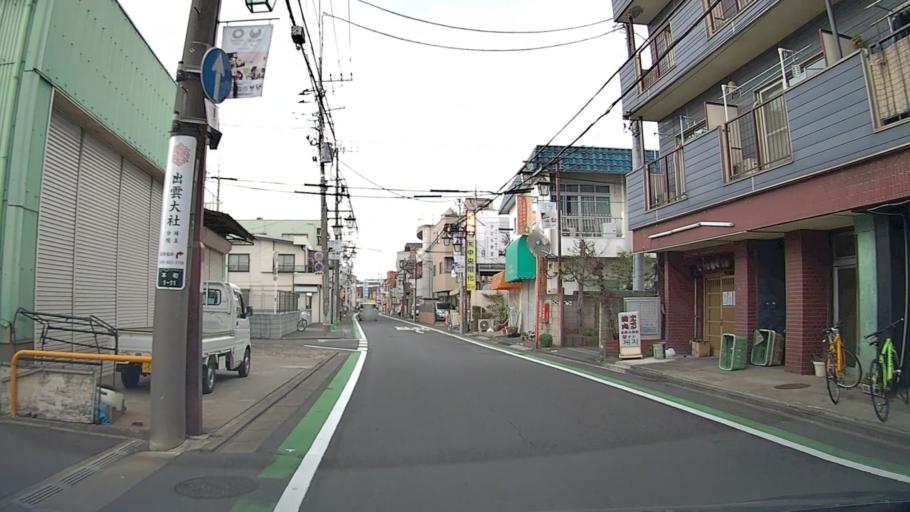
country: JP
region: Saitama
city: Asaka
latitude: 35.7991
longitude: 139.5958
